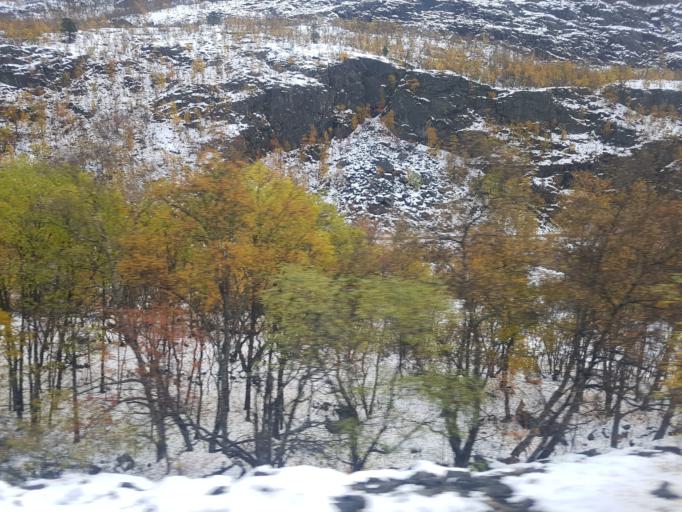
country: NO
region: Sor-Trondelag
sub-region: Oppdal
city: Oppdal
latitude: 62.3911
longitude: 9.6365
